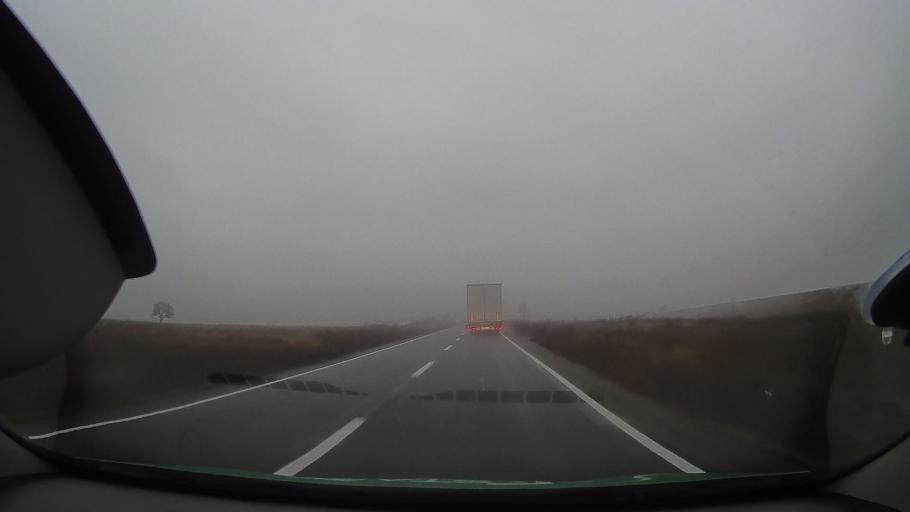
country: RO
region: Bihor
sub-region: Comuna Olcea
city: Olcea
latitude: 46.6654
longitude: 21.9633
